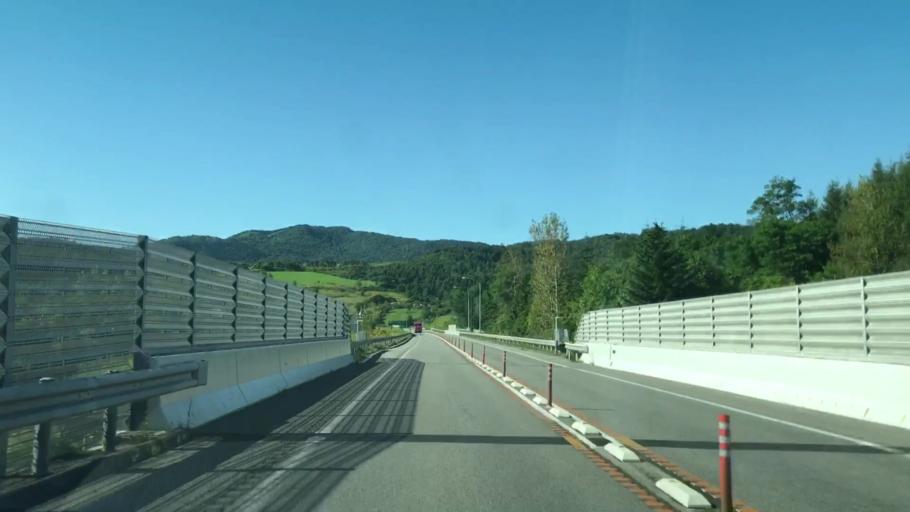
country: JP
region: Hokkaido
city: Date
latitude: 42.5460
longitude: 140.7927
